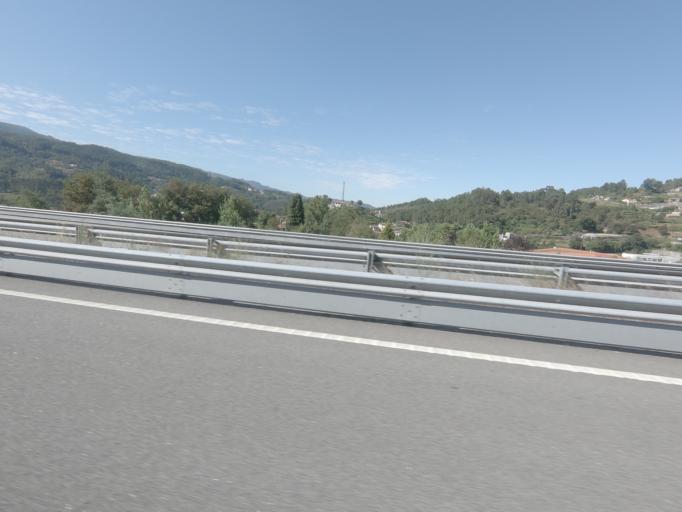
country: PT
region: Porto
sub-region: Amarante
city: Amarante
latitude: 41.2577
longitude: -8.0515
